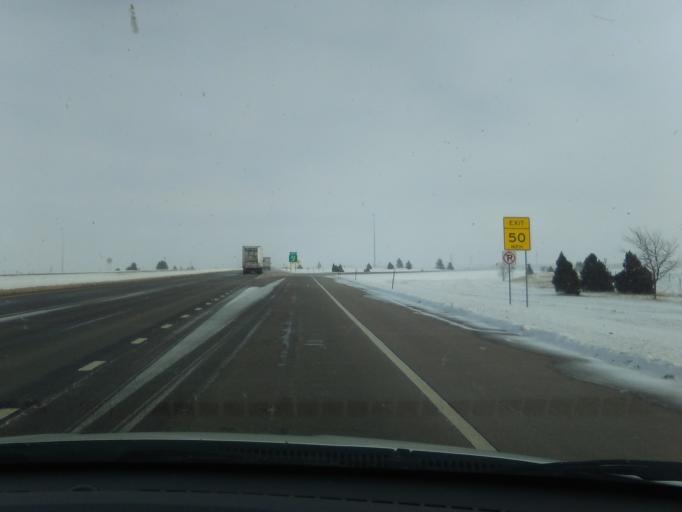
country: US
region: Nebraska
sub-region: Kimball County
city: Kimball
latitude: 41.2197
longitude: -103.6311
